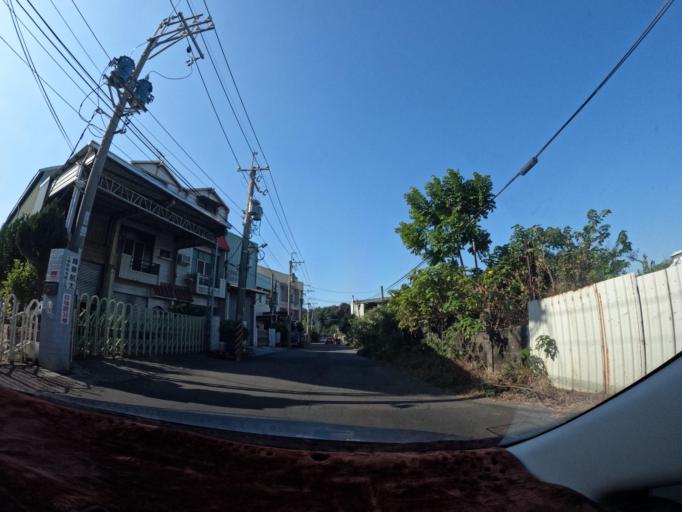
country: TW
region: Taiwan
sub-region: Tainan
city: Tainan
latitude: 23.0249
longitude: 120.2467
